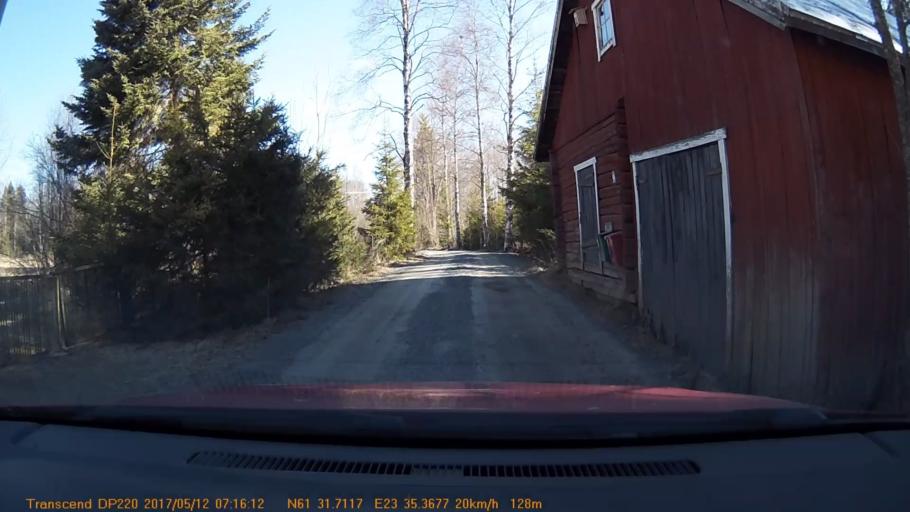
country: FI
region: Pirkanmaa
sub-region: Tampere
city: Yloejaervi
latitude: 61.5285
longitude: 23.5894
